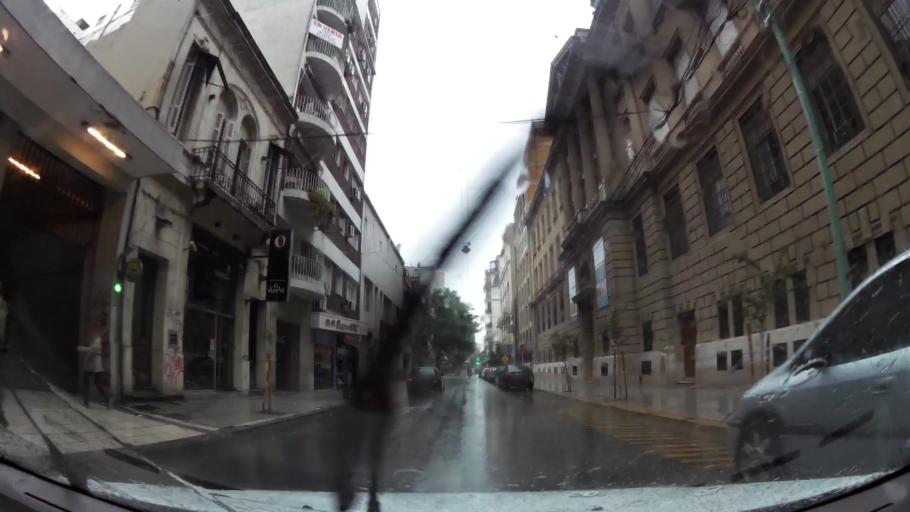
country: AR
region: Buenos Aires F.D.
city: Retiro
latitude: -34.5962
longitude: -58.3900
